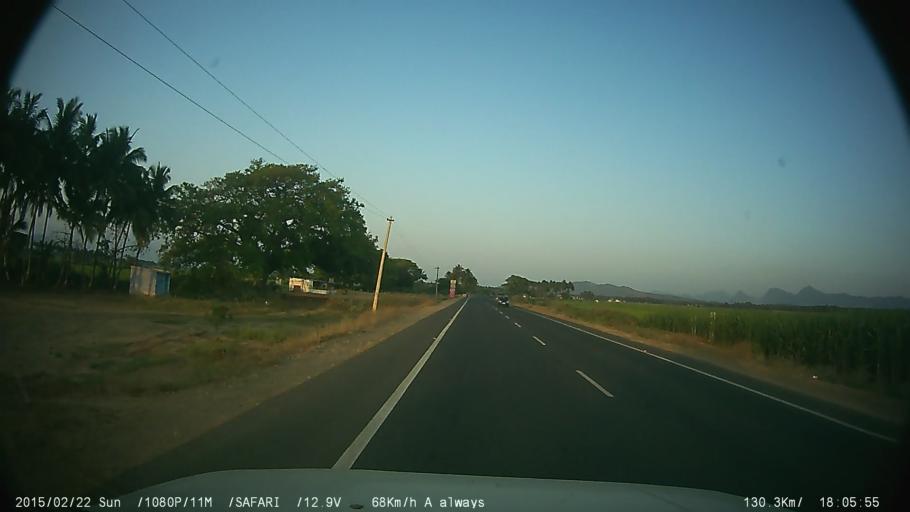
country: IN
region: Tamil Nadu
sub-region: Theni
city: Chinnamanur
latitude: 9.8260
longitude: 77.3607
